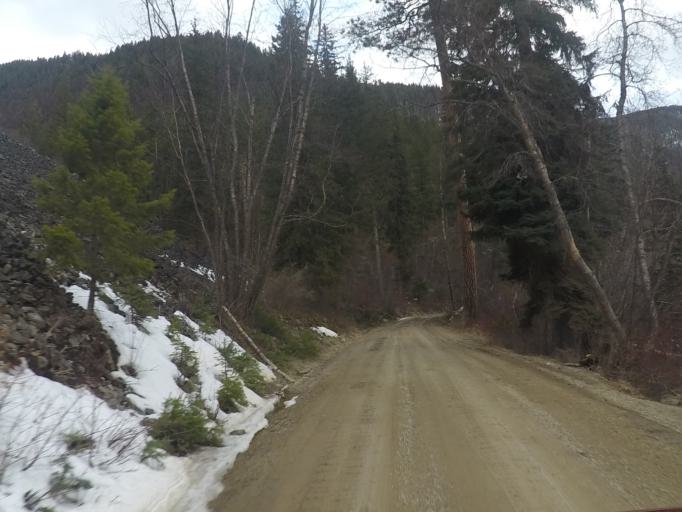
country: US
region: Montana
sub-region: Missoula County
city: Clinton
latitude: 46.5634
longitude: -113.7002
